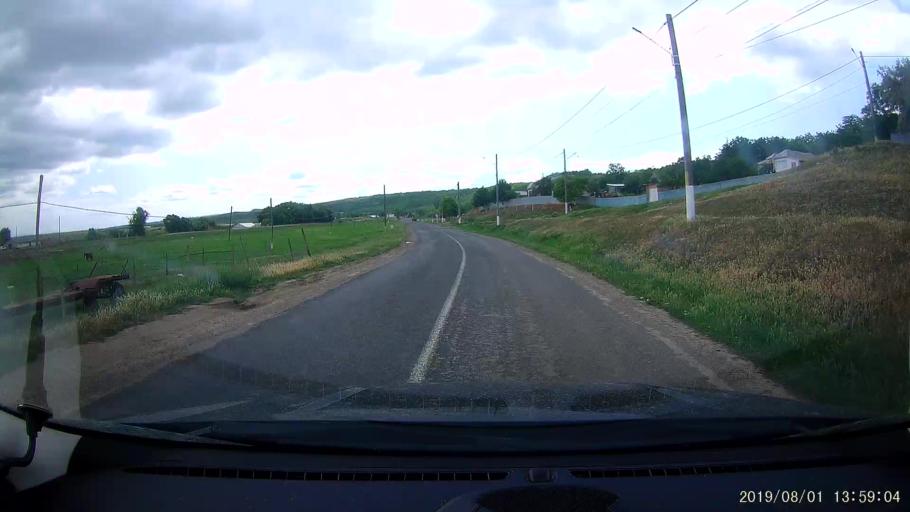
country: RO
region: Galati
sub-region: Comuna Foltesti
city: Foltesti
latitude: 45.7804
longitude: 28.0774
